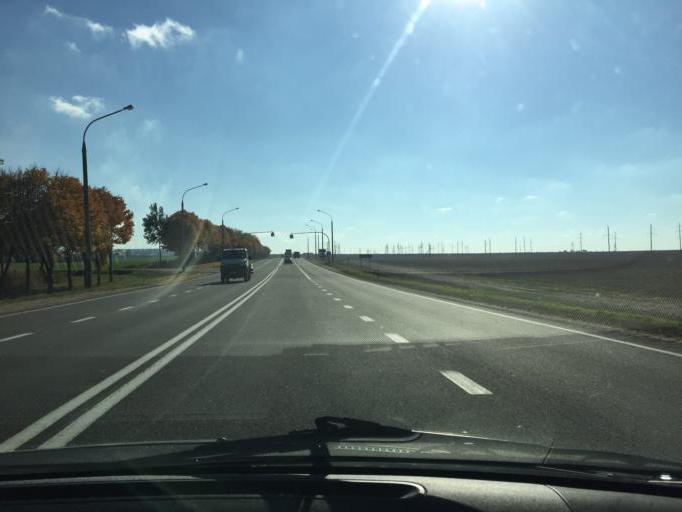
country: BY
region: Minsk
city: Salihorsk
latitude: 52.8722
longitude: 27.4673
